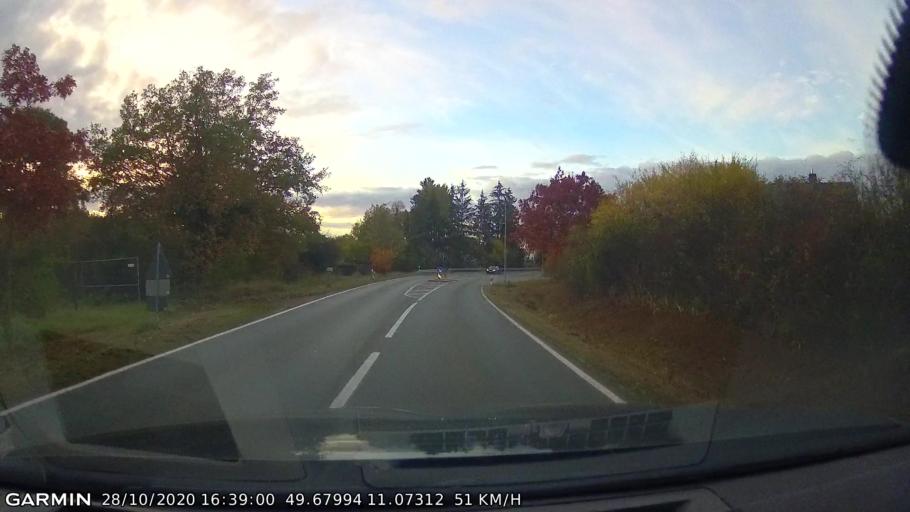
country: DE
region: Bavaria
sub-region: Upper Franconia
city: Poxdorf
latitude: 49.6800
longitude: 11.0730
